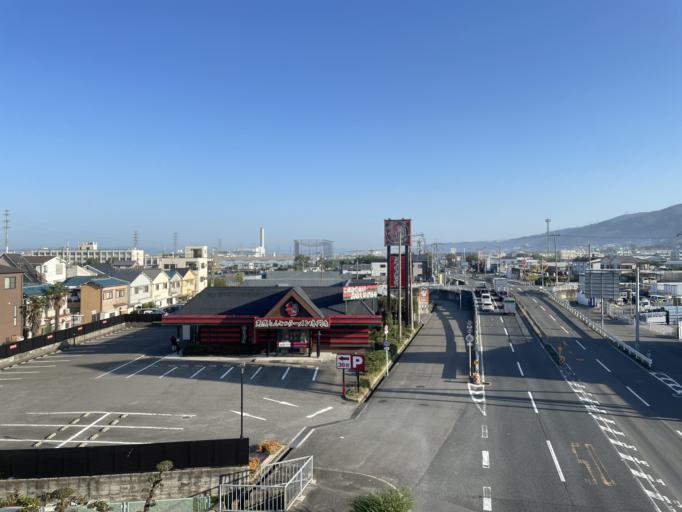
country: JP
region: Osaka
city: Yao
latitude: 34.6274
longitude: 135.6324
